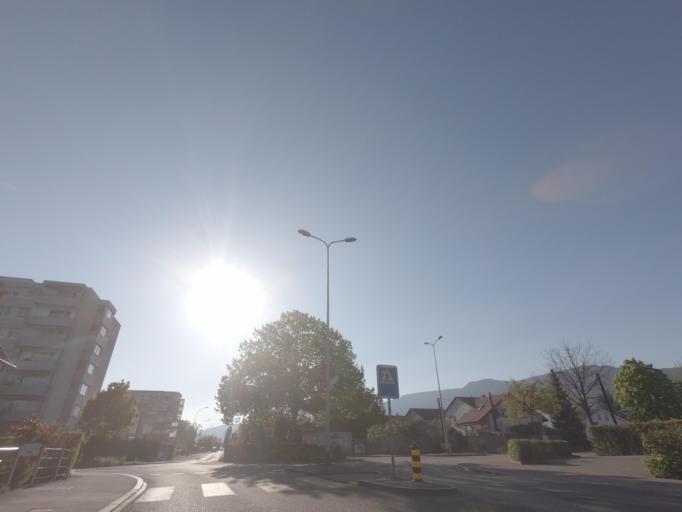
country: CH
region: Solothurn
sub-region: Bezirk Lebern
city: Langendorf
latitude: 47.2056
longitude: 7.5168
